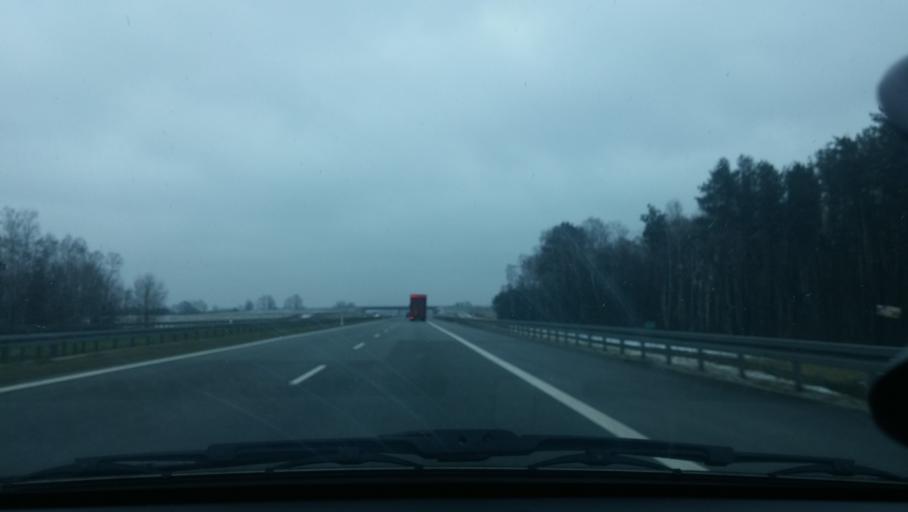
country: PL
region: Masovian Voivodeship
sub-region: Powiat minski
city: Jakubow
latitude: 52.2042
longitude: 21.6920
